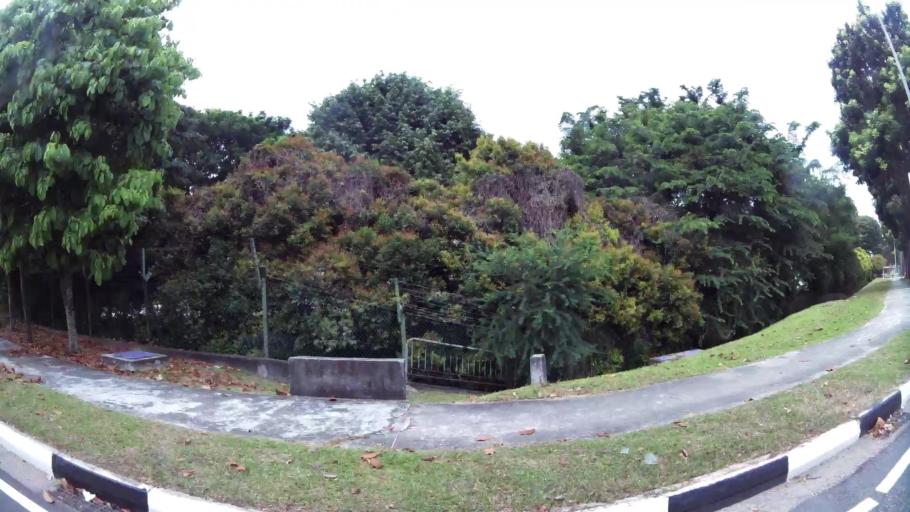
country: SG
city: Singapore
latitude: 1.3222
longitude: 103.7098
